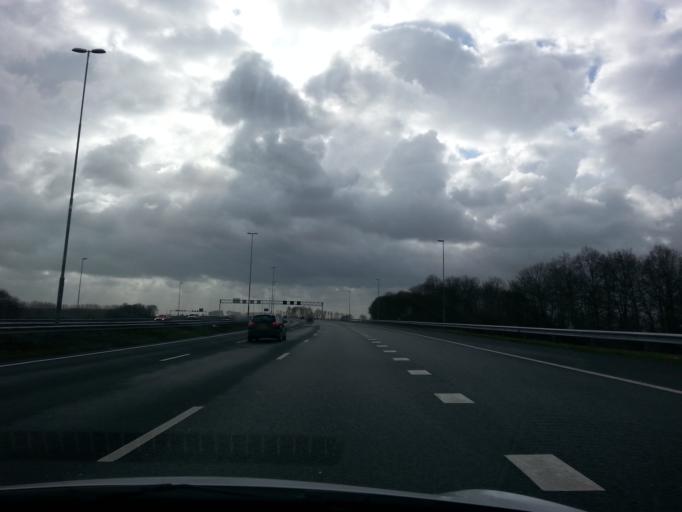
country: NL
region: Gelderland
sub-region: Gemeente Maasdriel
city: Hedel
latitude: 51.7715
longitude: 5.2614
